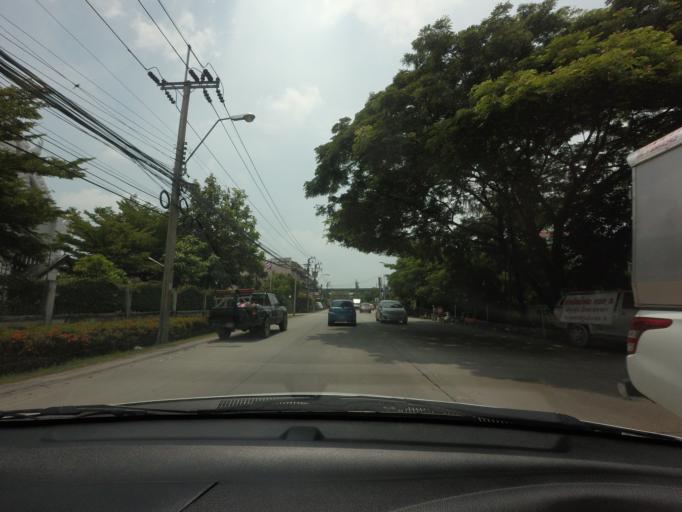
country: TH
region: Bangkok
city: Bang Na
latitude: 13.6555
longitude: 100.6776
